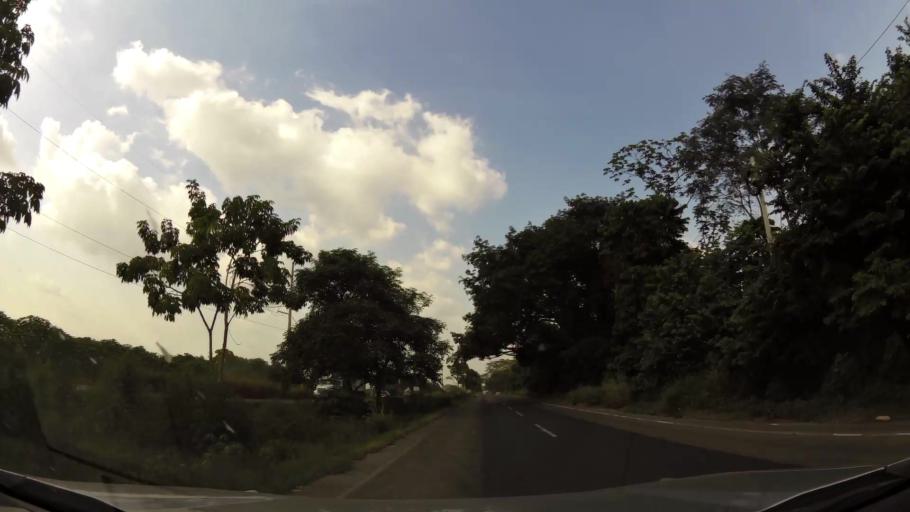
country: GT
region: Escuintla
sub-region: Municipio de Masagua
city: Masagua
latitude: 14.0753
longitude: -90.7775
